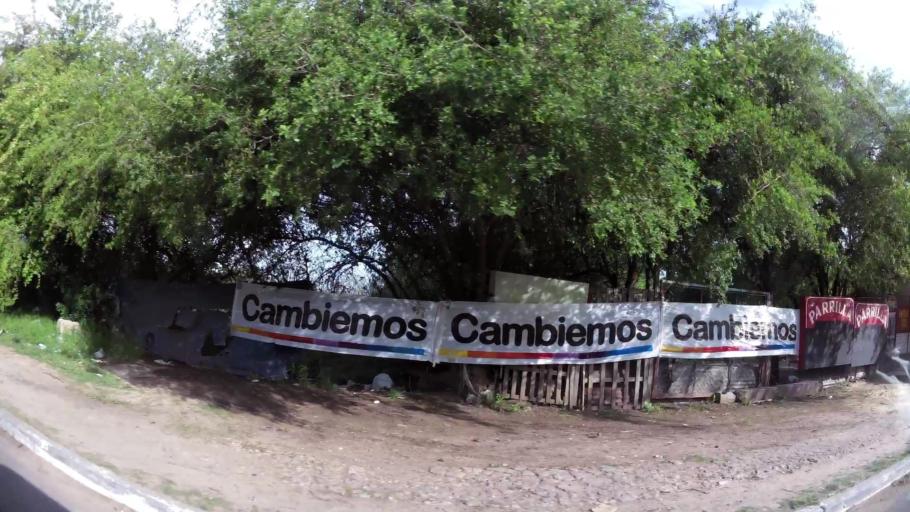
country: AR
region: Buenos Aires
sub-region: Partido de Quilmes
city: Quilmes
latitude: -34.7474
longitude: -58.2690
